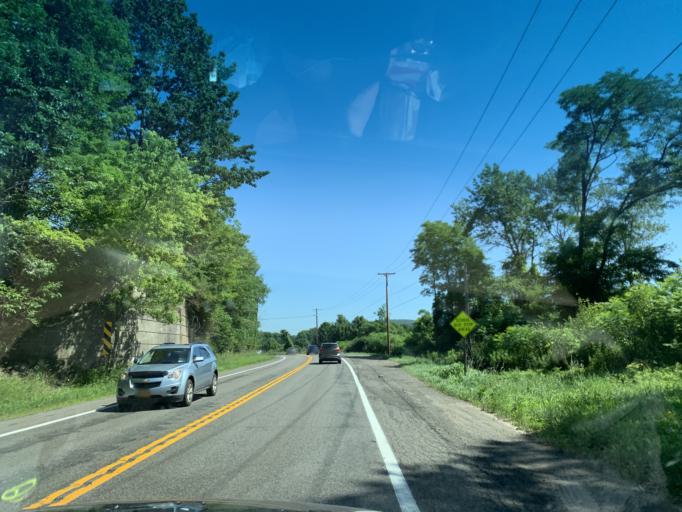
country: US
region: New York
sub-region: Delaware County
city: Sidney
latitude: 42.3284
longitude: -75.4095
